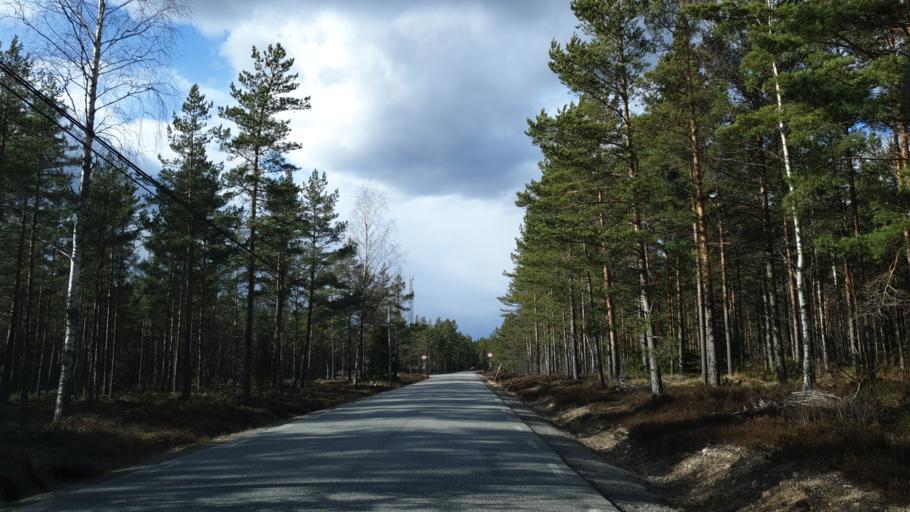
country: SE
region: Stockholm
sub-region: Tyreso Kommun
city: Brevik
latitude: 59.2517
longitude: 18.4389
